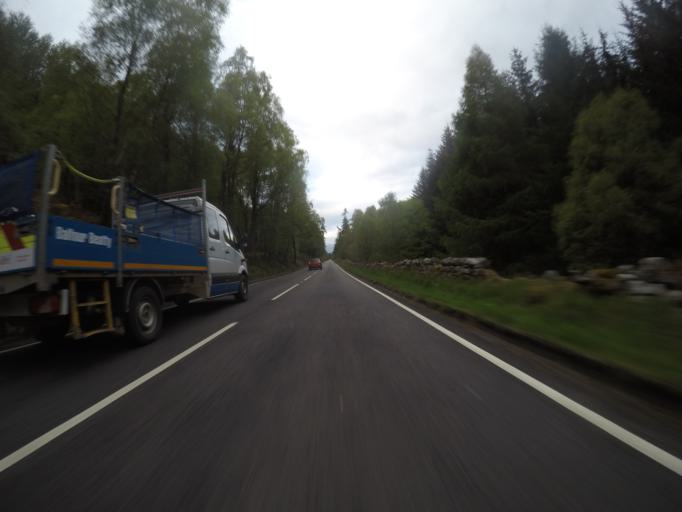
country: GB
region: Scotland
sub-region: Highland
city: Spean Bridge
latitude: 57.1185
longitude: -4.7021
